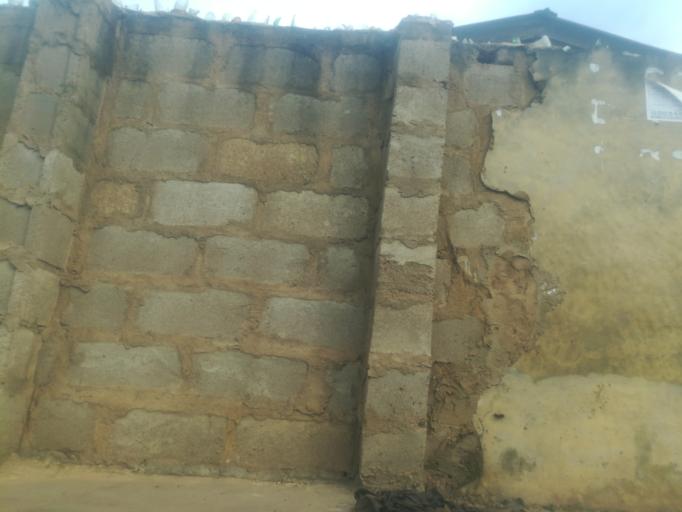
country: NG
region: Oyo
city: Ibadan
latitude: 7.3817
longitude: 3.9333
